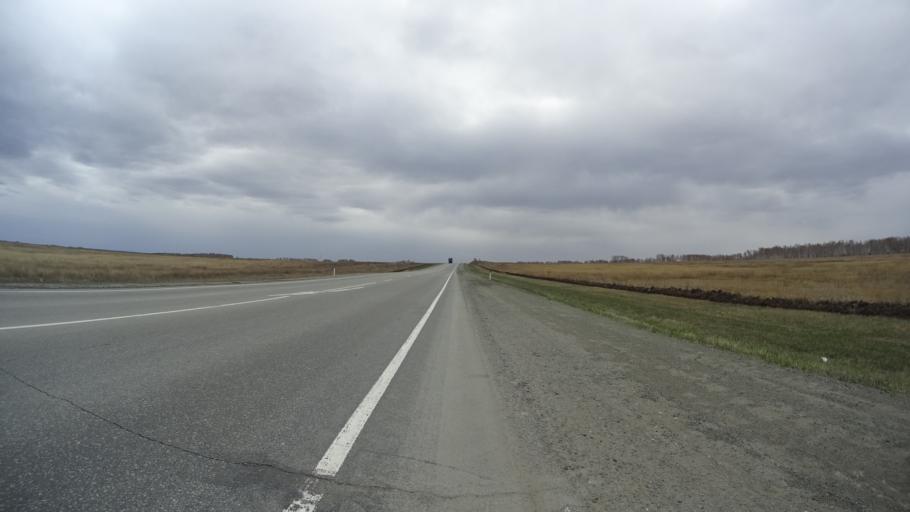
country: RU
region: Chelyabinsk
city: Yemanzhelinsk
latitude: 54.7098
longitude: 61.2593
